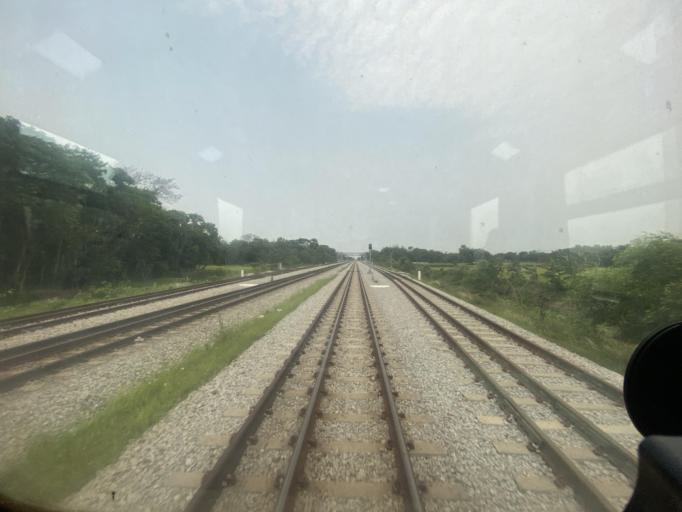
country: BD
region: Chittagong
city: Laksham
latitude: 23.3025
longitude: 91.1374
